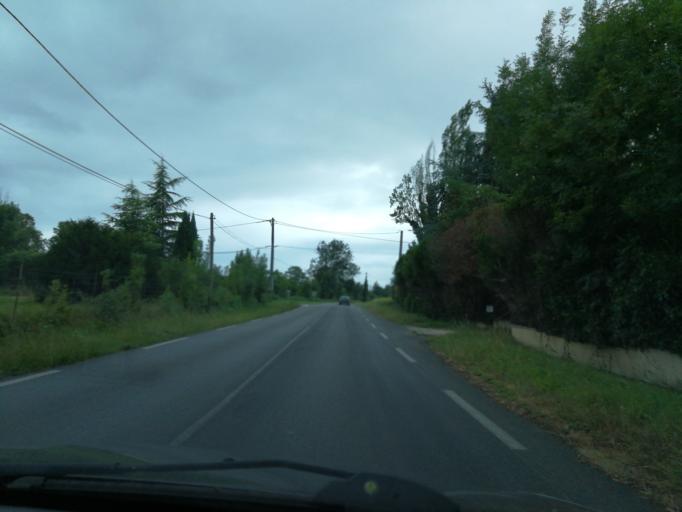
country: FR
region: Midi-Pyrenees
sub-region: Departement des Hautes-Pyrenees
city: Bazet
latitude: 43.2681
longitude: 0.0772
